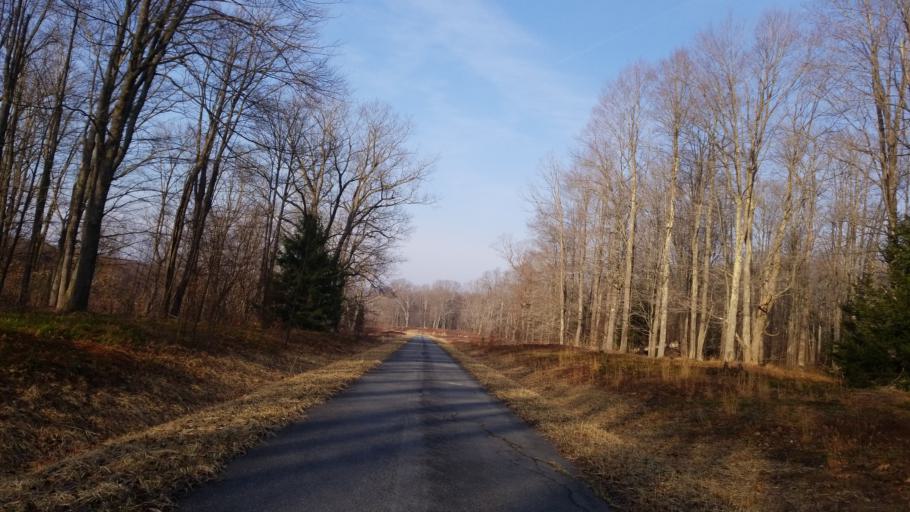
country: US
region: Pennsylvania
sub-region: Clearfield County
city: Shiloh
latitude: 41.2245
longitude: -78.2303
